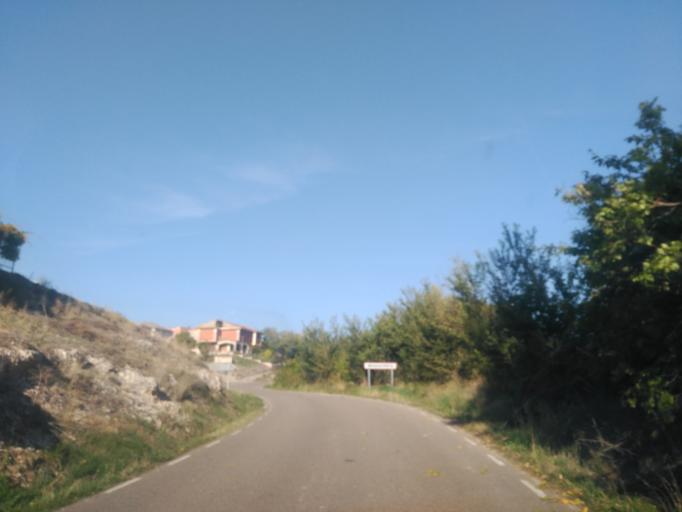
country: ES
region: Castille and Leon
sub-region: Provincia de Burgos
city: Brazacorta
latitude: 41.7159
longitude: -3.3682
